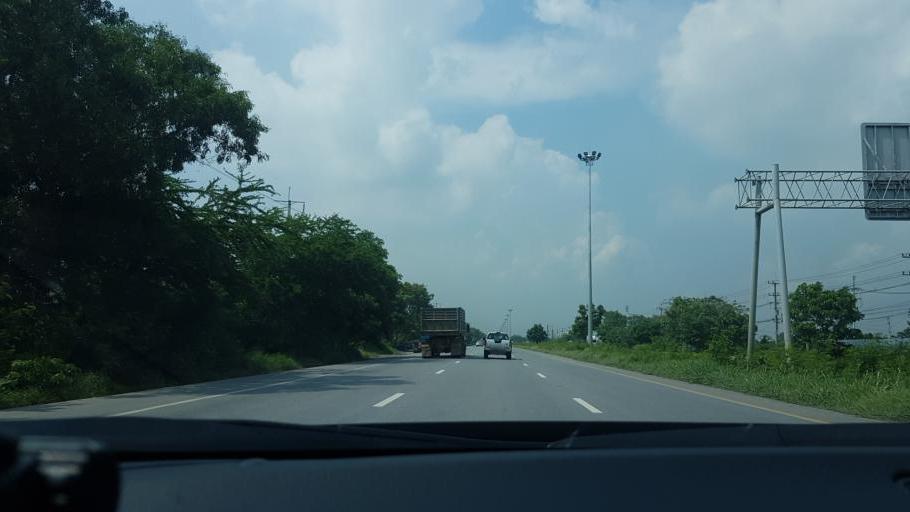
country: TH
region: Pathum Thani
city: Sam Khok
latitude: 14.0959
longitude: 100.5705
